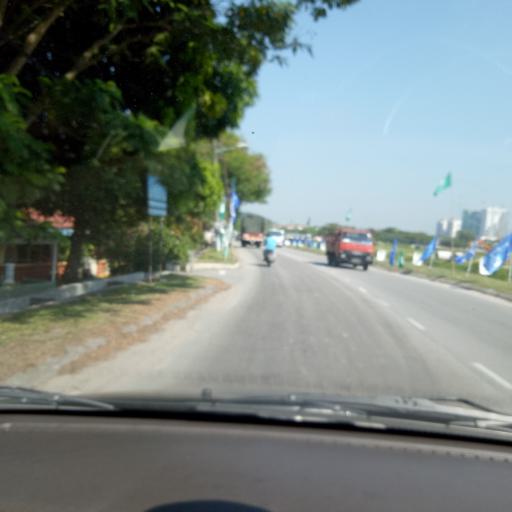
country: MY
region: Selangor
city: Kampong Baharu Balakong
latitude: 3.0149
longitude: 101.7672
